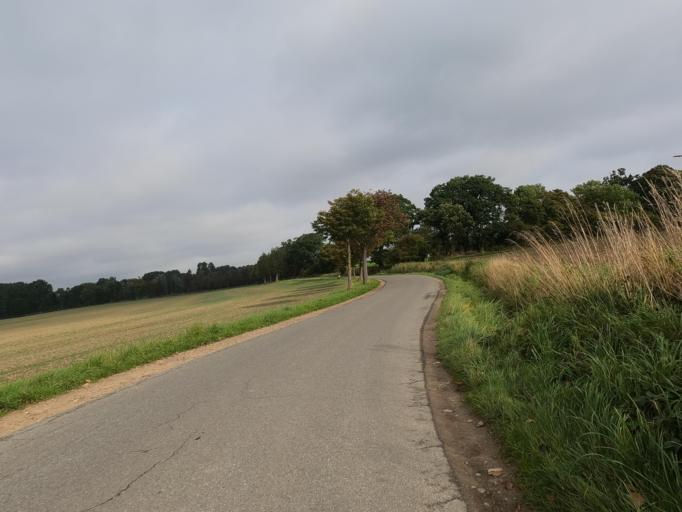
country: DE
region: Schleswig-Holstein
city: Grube
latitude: 54.2800
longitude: 11.0528
